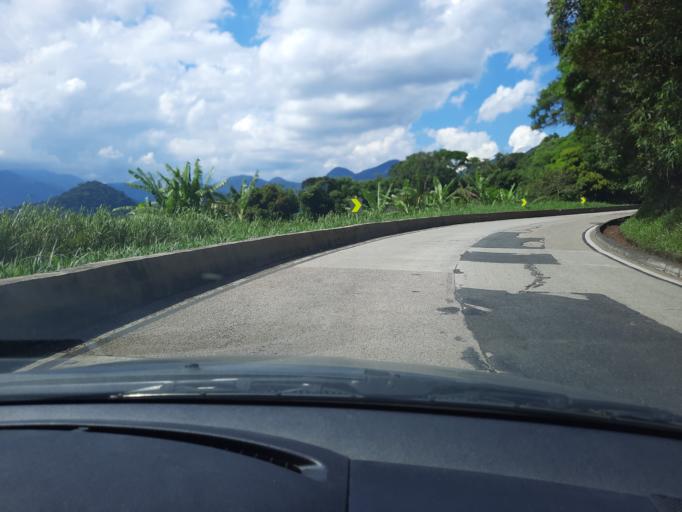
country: BR
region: Rio de Janeiro
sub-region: Petropolis
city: Petropolis
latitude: -22.5747
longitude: -43.2612
